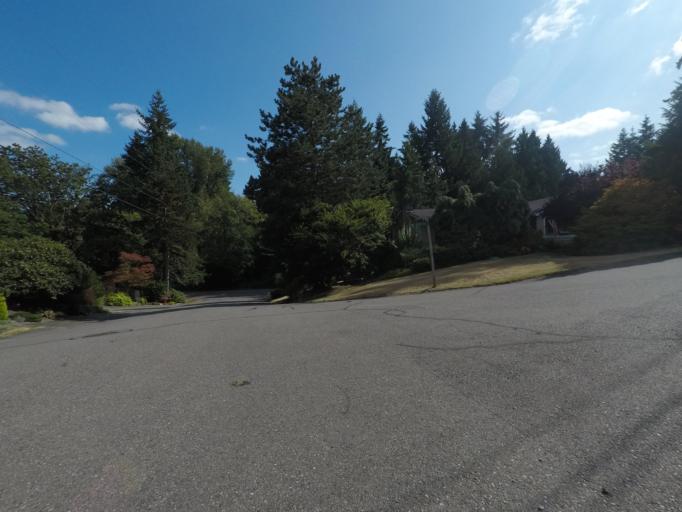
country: US
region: Washington
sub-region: Snohomish County
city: Brier
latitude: 47.7753
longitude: -122.2578
